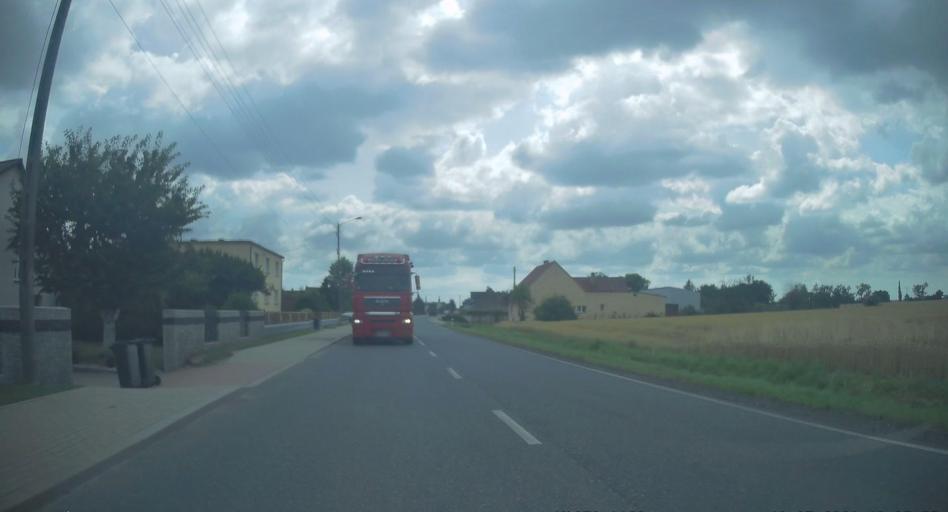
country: PL
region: Opole Voivodeship
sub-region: Powiat prudnicki
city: Glogowek
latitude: 50.3444
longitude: 17.8992
